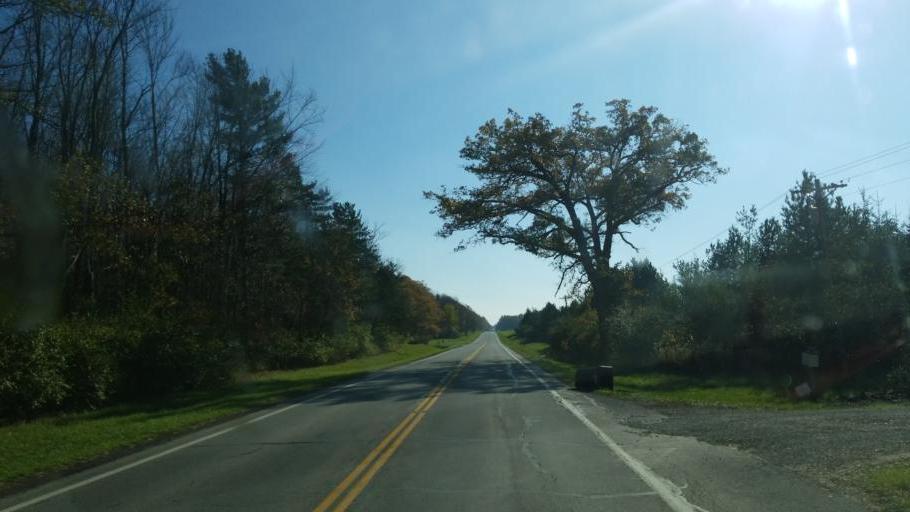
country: US
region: Ohio
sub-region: Lorain County
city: Wellington
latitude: 41.1357
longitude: -82.2190
